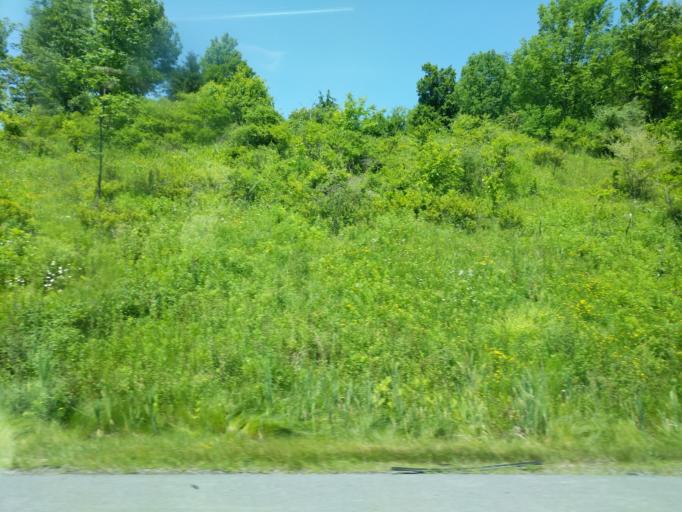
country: US
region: New York
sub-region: Sullivan County
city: Livingston Manor
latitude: 41.9244
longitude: -74.8595
